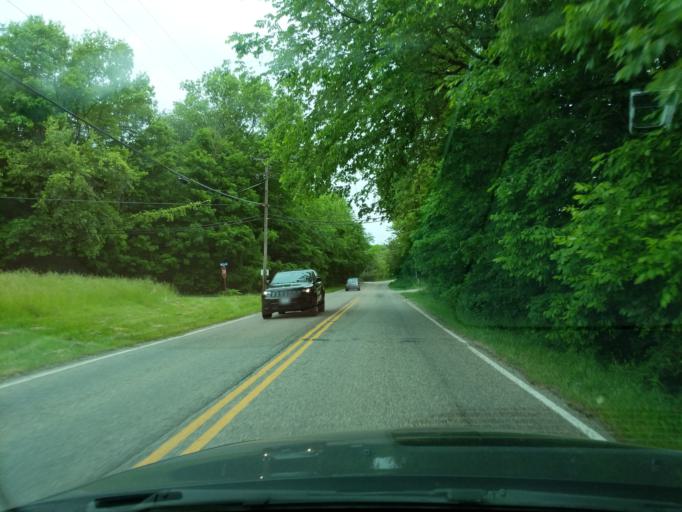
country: US
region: Ohio
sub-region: Stark County
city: Massillon
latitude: 40.7780
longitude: -81.5710
